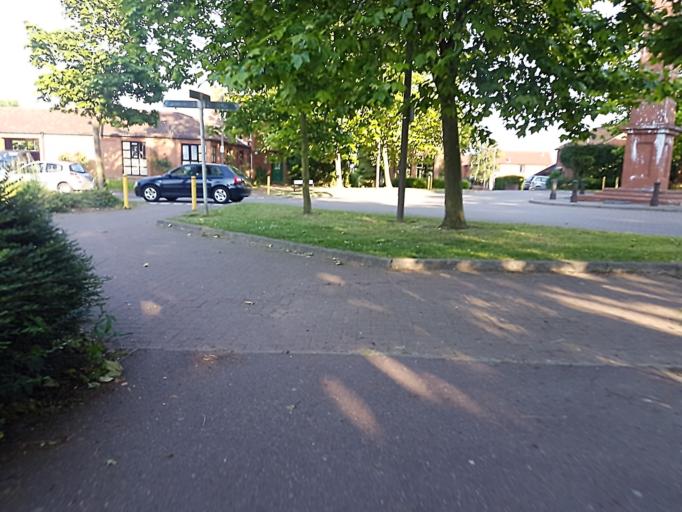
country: GB
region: England
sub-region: Milton Keynes
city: Loughton
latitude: 52.0340
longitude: -0.7939
